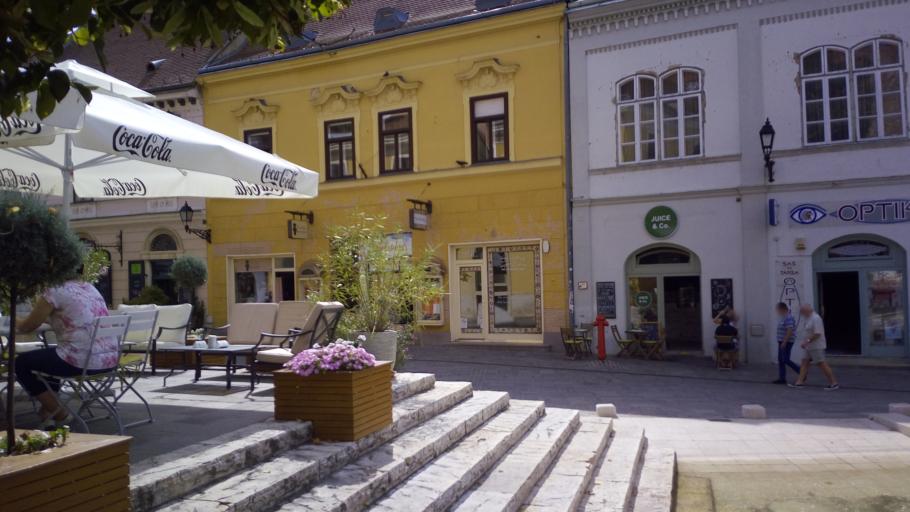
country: HU
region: Baranya
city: Pecs
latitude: 46.0755
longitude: 18.2273
